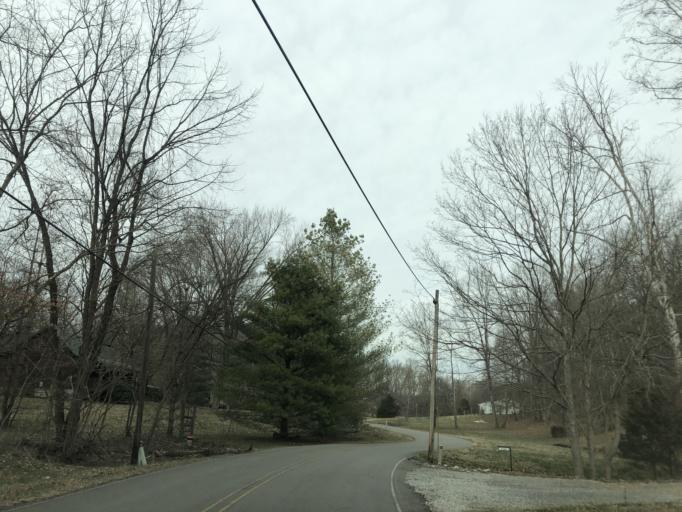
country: US
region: Tennessee
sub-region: Robertson County
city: Greenbrier
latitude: 36.4732
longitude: -86.7983
